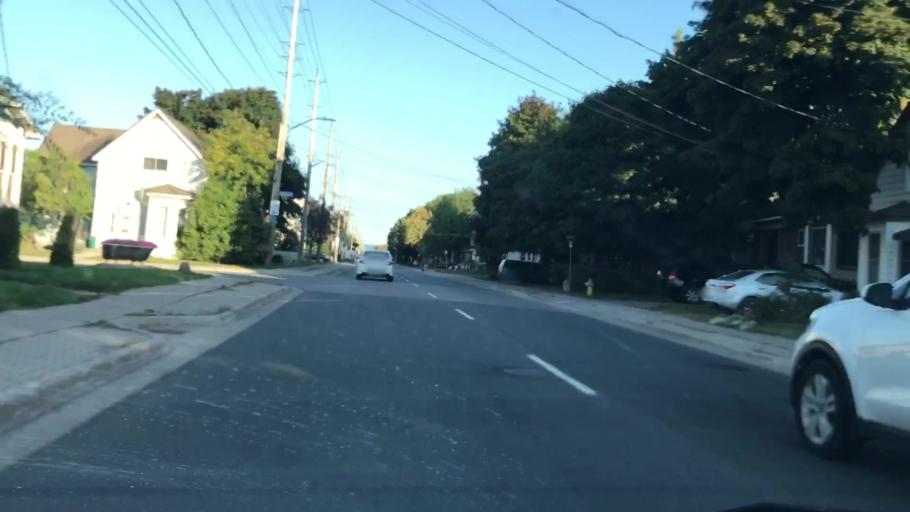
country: CA
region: Ontario
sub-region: Algoma
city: Sault Ste. Marie
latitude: 46.5124
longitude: -84.3292
